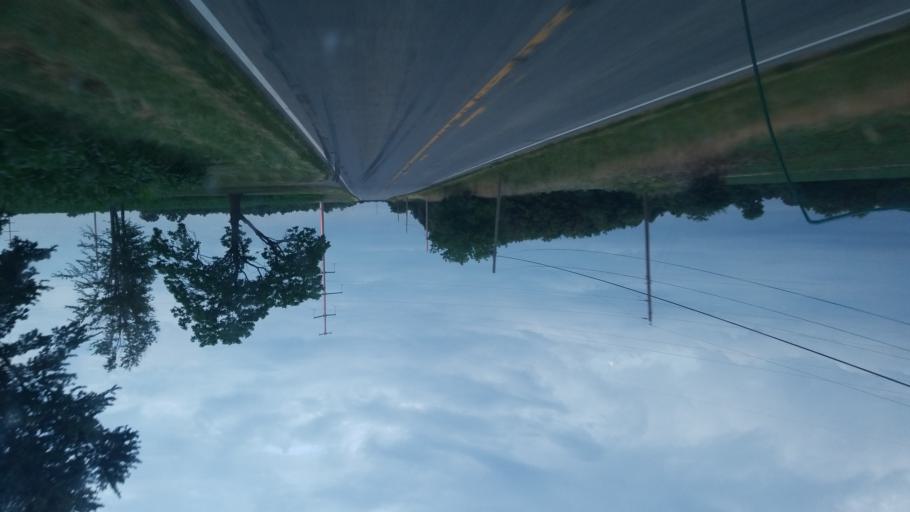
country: US
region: Ohio
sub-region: Defiance County
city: Hicksville
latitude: 41.3377
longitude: -84.8230
